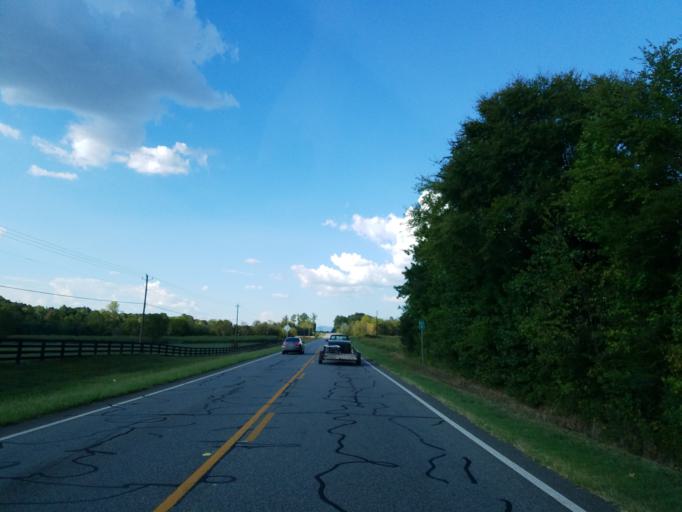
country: US
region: Georgia
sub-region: Bartow County
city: Rydal
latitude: 34.5248
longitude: -84.7067
